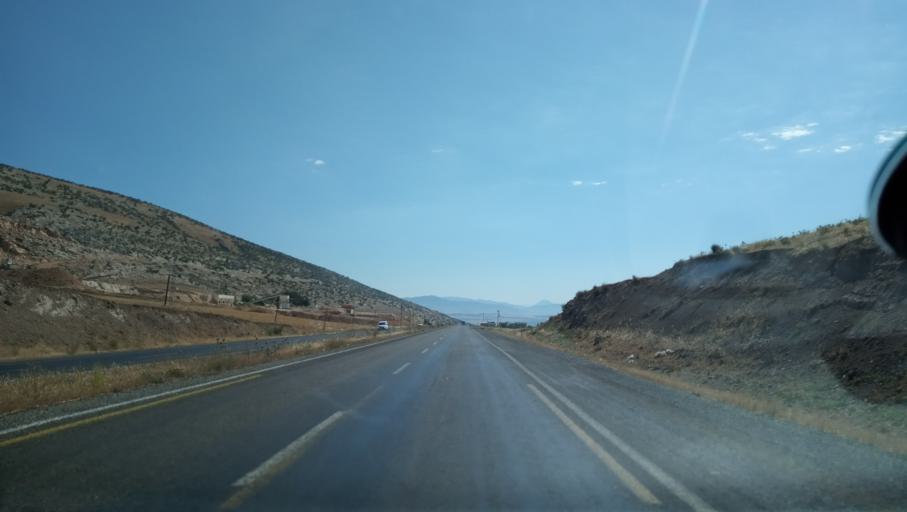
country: TR
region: Diyarbakir
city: Malabadi
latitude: 38.1220
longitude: 41.1538
